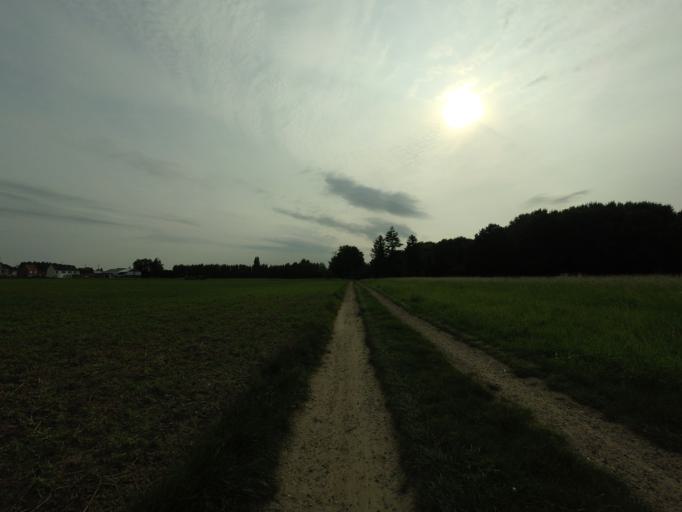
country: BE
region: Flanders
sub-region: Provincie Vlaams-Brabant
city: Kampenhout
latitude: 50.9354
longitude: 4.5369
